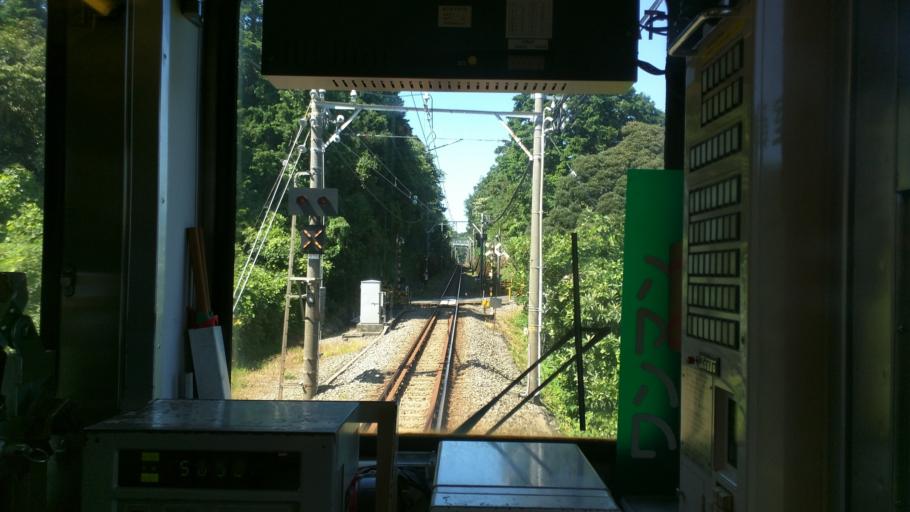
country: JP
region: Shizuoka
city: Ito
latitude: 34.9305
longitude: 139.1363
